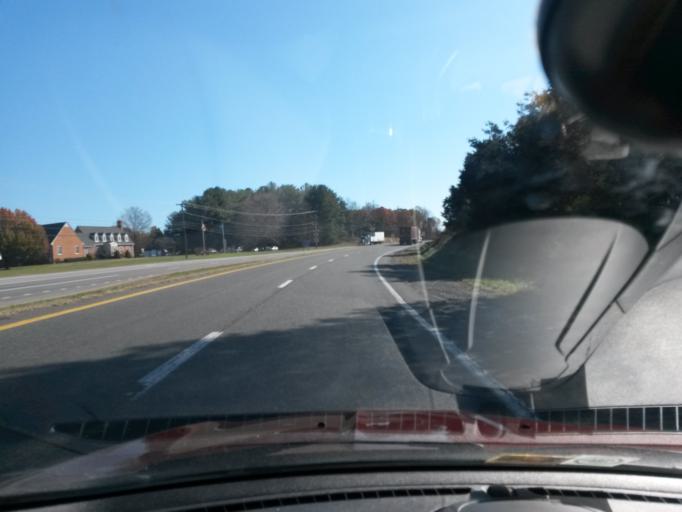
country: US
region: Virginia
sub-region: City of Bedford
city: Bedford
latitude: 37.3189
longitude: -79.4840
